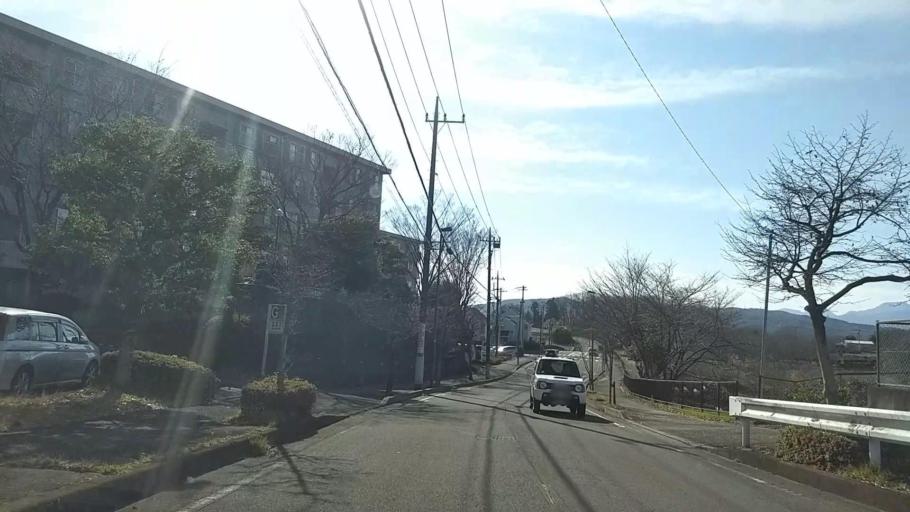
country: JP
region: Kanagawa
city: Hadano
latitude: 35.3552
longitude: 139.2236
